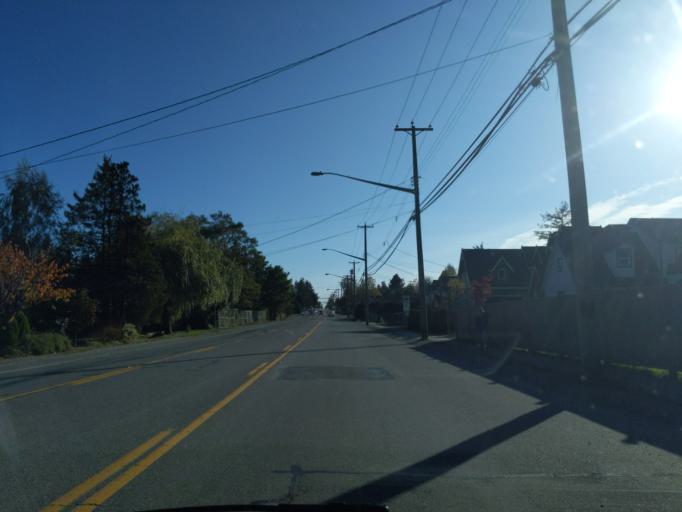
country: CA
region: British Columbia
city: New Westminster
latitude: 49.2007
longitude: -122.8565
